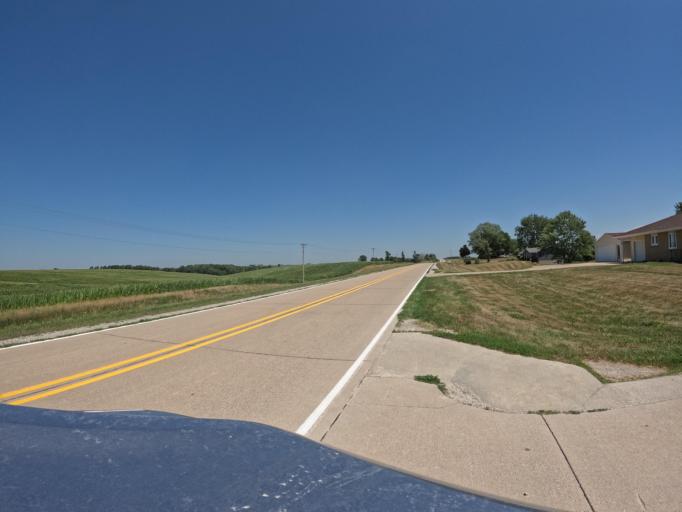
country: US
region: Iowa
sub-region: Poweshiek County
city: Montezuma
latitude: 41.4810
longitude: -92.3896
